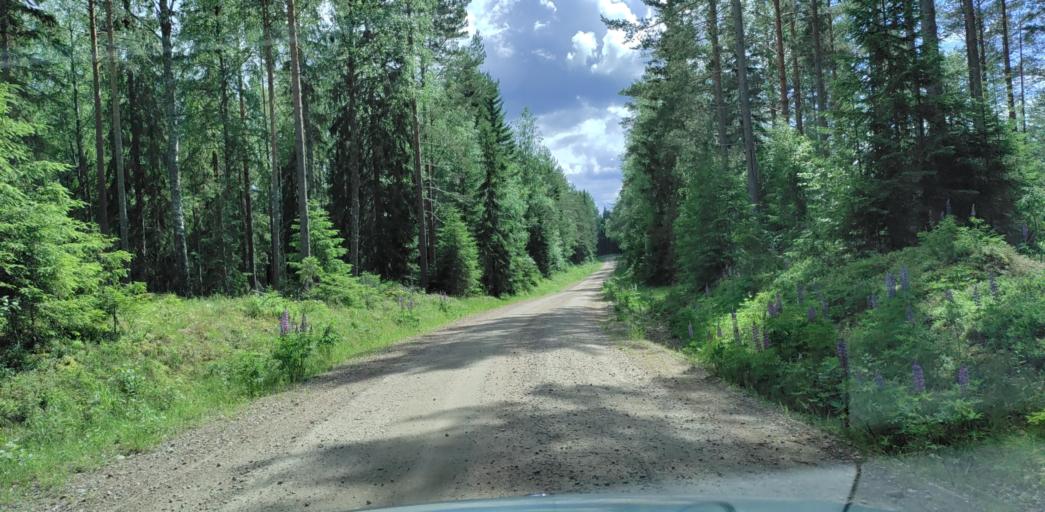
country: SE
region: Vaermland
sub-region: Hagfors Kommun
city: Ekshaerad
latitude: 60.0586
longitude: 13.3109
